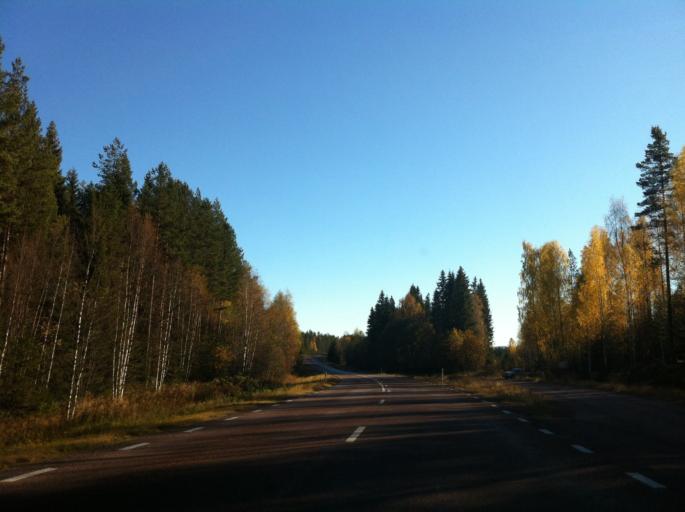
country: SE
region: Dalarna
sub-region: Alvdalens Kommun
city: AElvdalen
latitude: 61.1723
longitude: 14.1042
